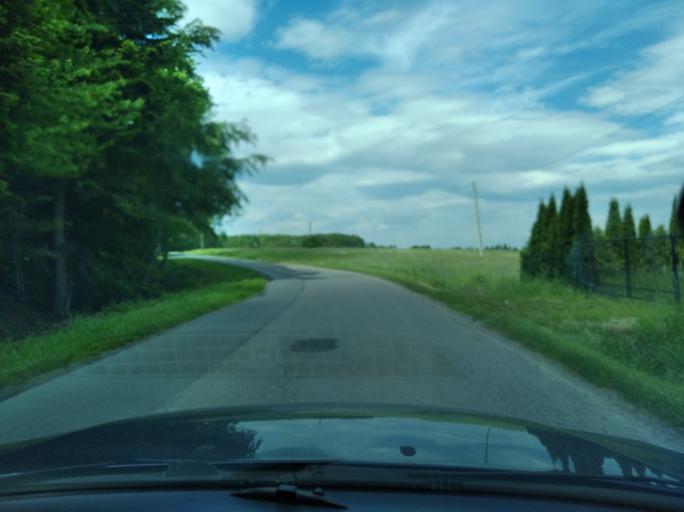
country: PL
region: Subcarpathian Voivodeship
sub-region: Powiat ropczycko-sedziszowski
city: Ropczyce
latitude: 50.0148
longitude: 21.6108
